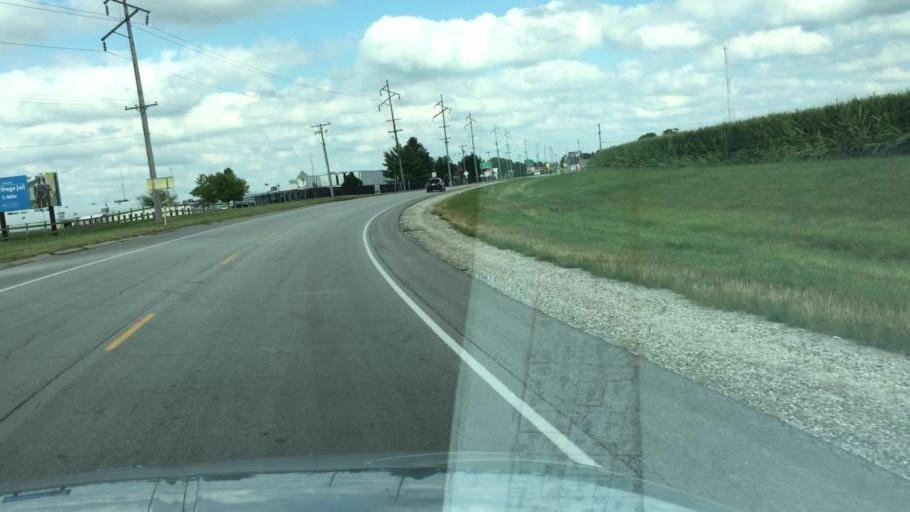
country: US
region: Illinois
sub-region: Hancock County
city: Carthage
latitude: 40.4162
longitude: -91.1524
